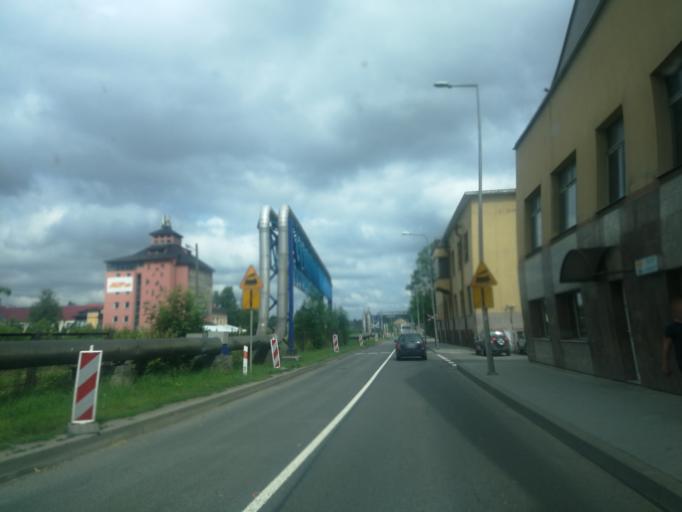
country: PL
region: Subcarpathian Voivodeship
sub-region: Powiat sanocki
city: Sanok
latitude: 49.5496
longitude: 22.2177
